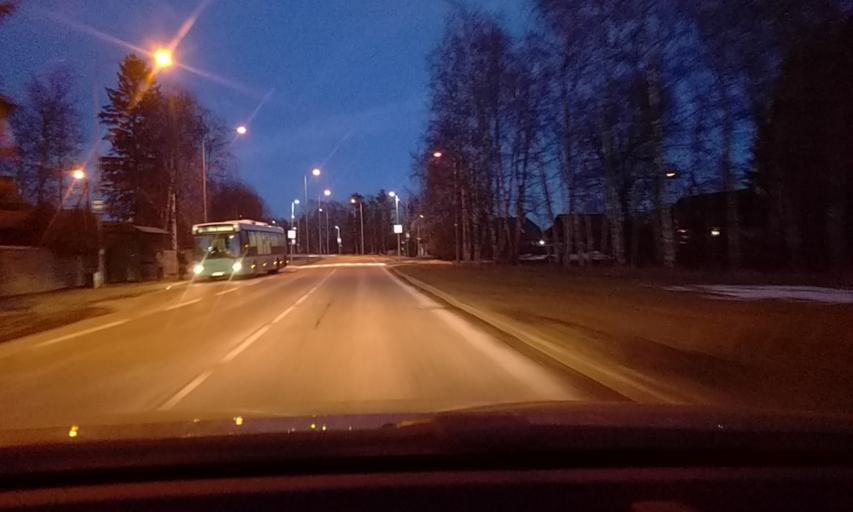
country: EE
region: Harju
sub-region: Viimsi vald
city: Viimsi
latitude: 59.4870
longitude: 24.8649
